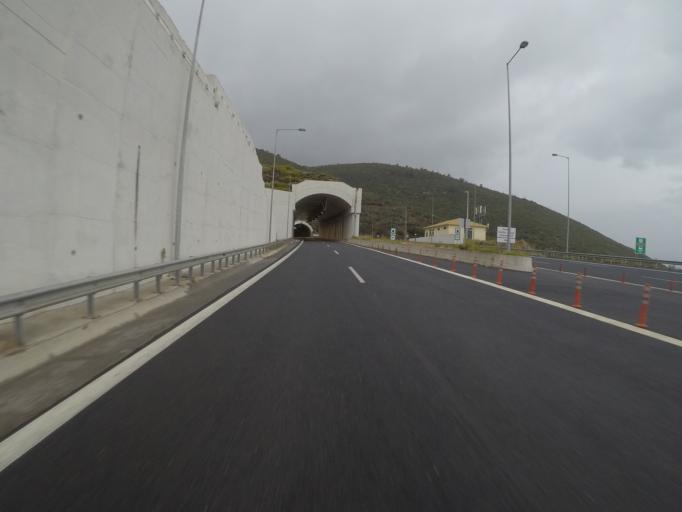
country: GR
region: Peloponnese
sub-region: Nomos Arkadias
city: Megalopoli
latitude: 37.3856
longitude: 22.1945
